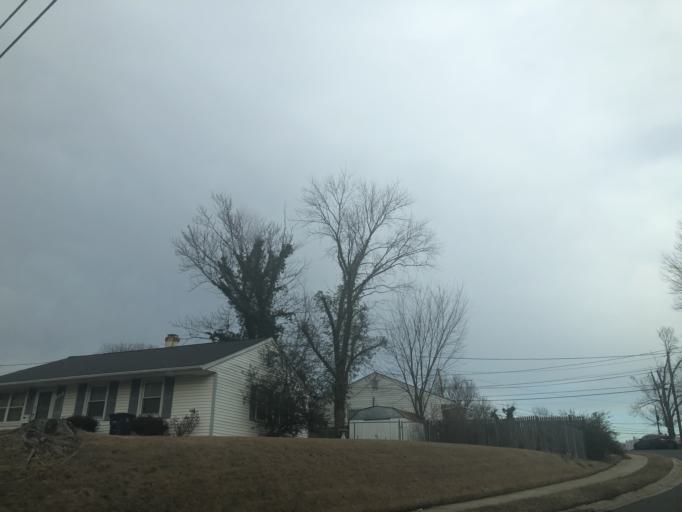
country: US
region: Maryland
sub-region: Prince George's County
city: Oxon Hill
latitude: 38.7931
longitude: -76.9947
